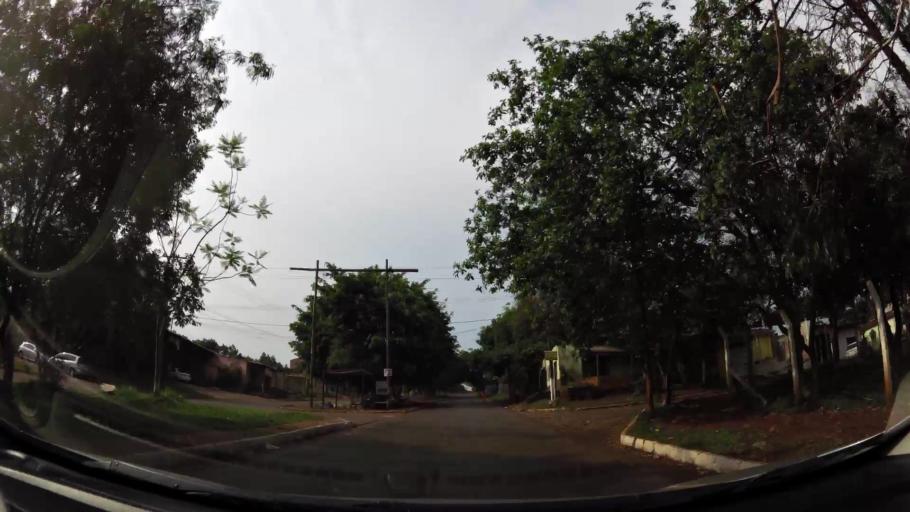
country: PY
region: Alto Parana
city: Ciudad del Este
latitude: -25.4926
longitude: -54.6488
